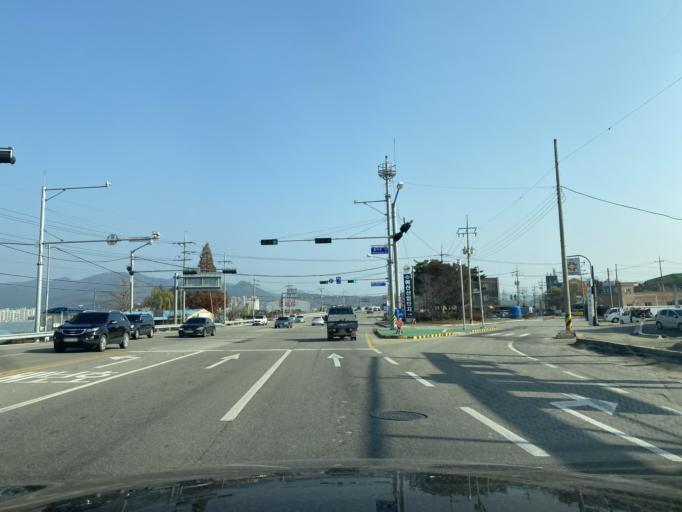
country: KR
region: Chungcheongnam-do
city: Yesan
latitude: 36.6849
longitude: 126.8154
